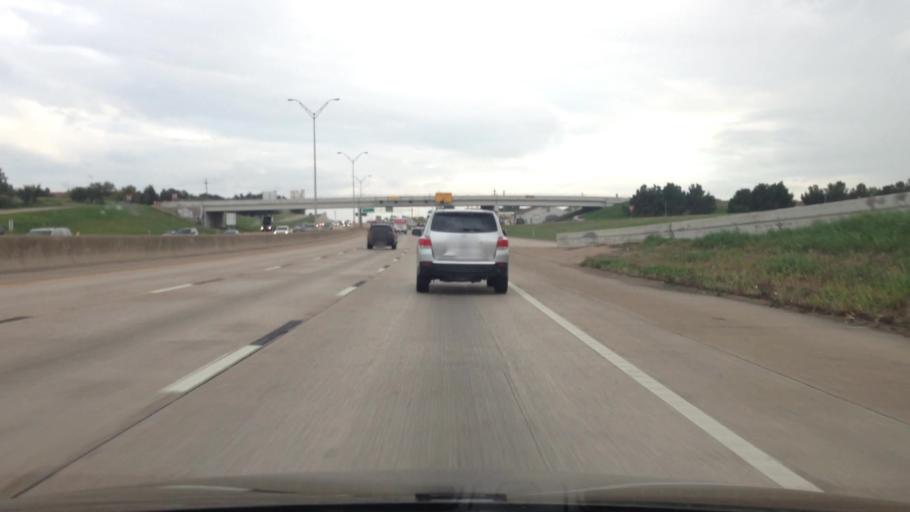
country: US
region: Texas
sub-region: Tarrant County
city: Edgecliff Village
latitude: 32.6627
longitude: -97.3212
